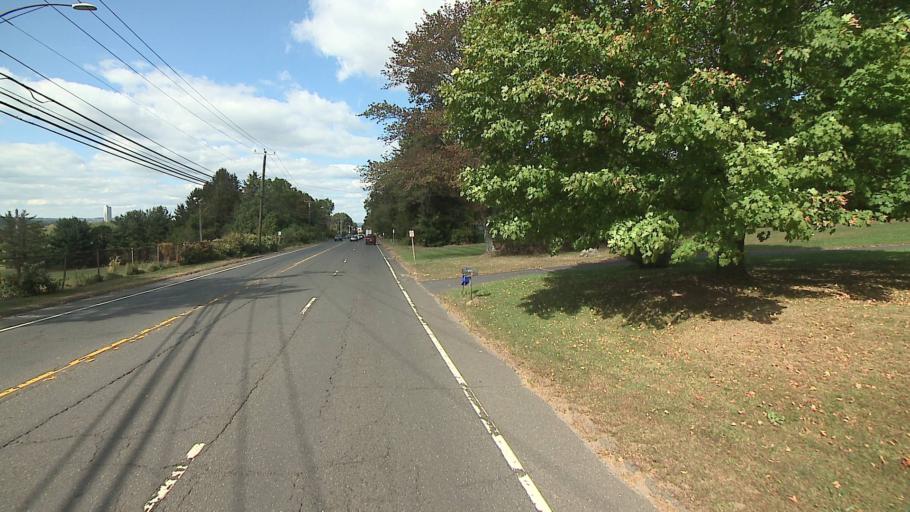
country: US
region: Connecticut
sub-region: Hartford County
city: Plainville
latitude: 41.6357
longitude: -72.9002
